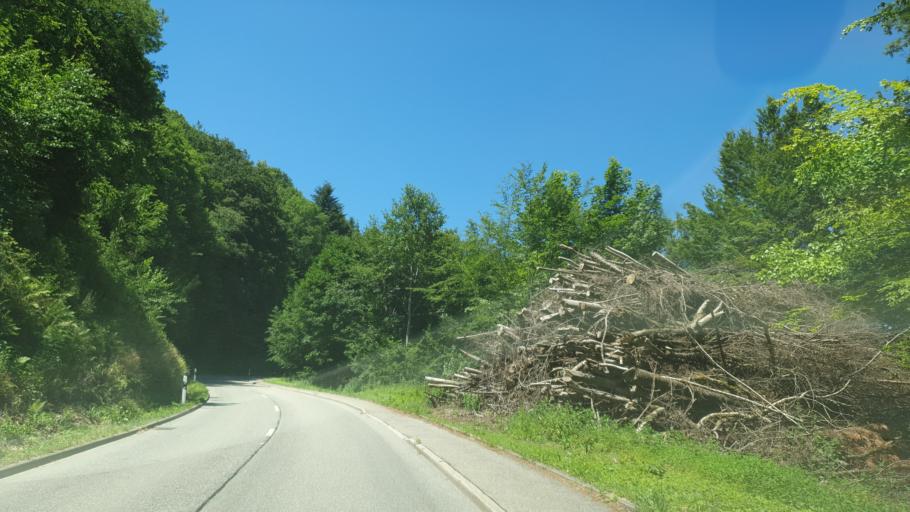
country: DE
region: Baden-Wuerttemberg
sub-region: Freiburg Region
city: Horben
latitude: 47.9411
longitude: 7.8624
